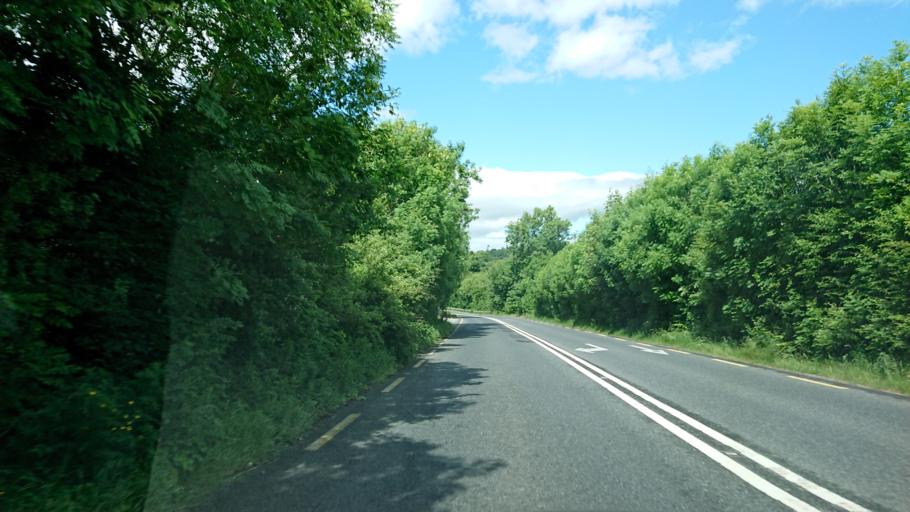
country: IE
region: Leinster
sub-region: Kilkenny
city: Mooncoin
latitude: 52.2325
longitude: -7.2111
